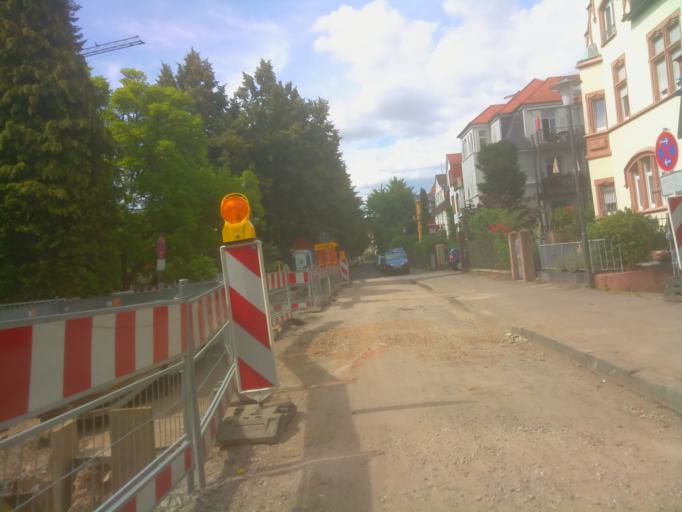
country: DE
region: Baden-Wuerttemberg
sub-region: Karlsruhe Region
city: Heidelberg
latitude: 49.4189
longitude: 8.6872
